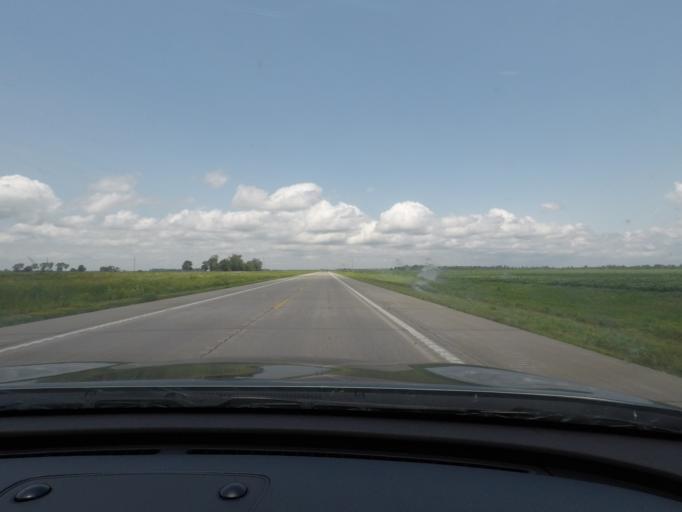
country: US
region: Missouri
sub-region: Carroll County
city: Carrollton
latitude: 39.2238
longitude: -93.5127
